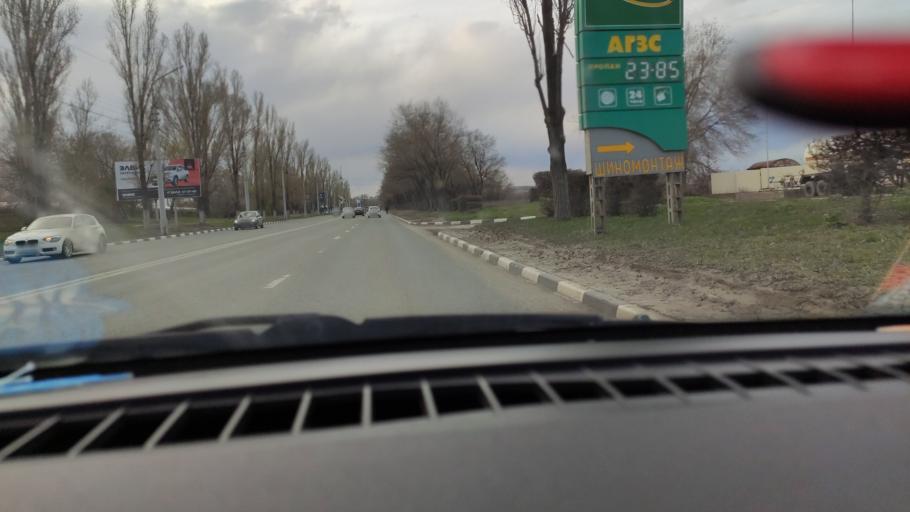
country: RU
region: Saratov
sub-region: Saratovskiy Rayon
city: Saratov
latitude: 51.5777
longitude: 45.9863
